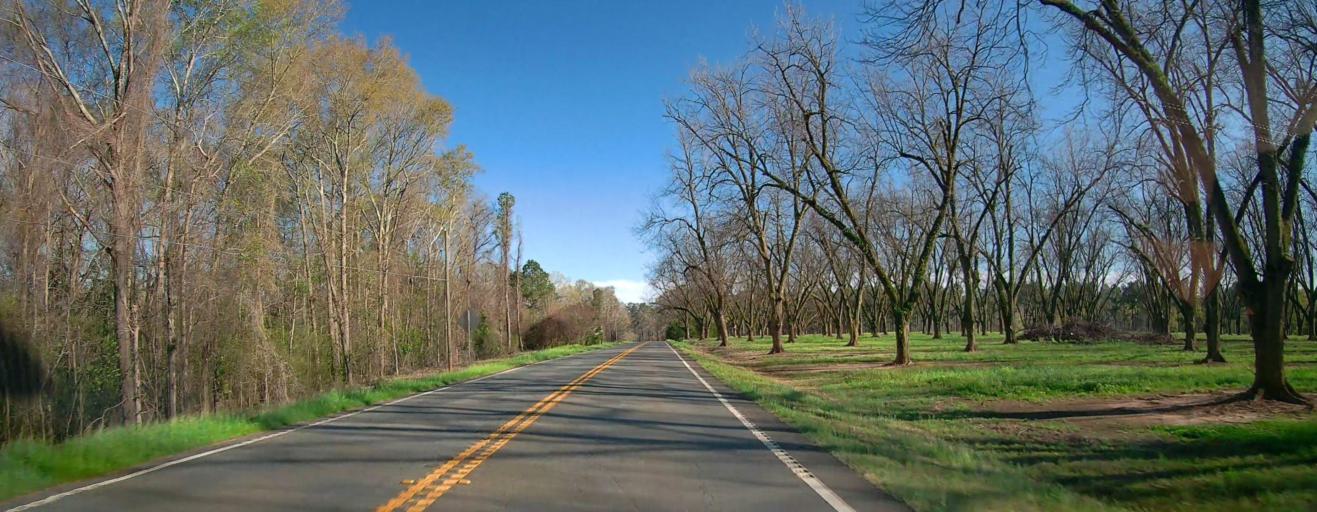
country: US
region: Georgia
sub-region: Macon County
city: Marshallville
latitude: 32.4532
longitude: -83.9126
